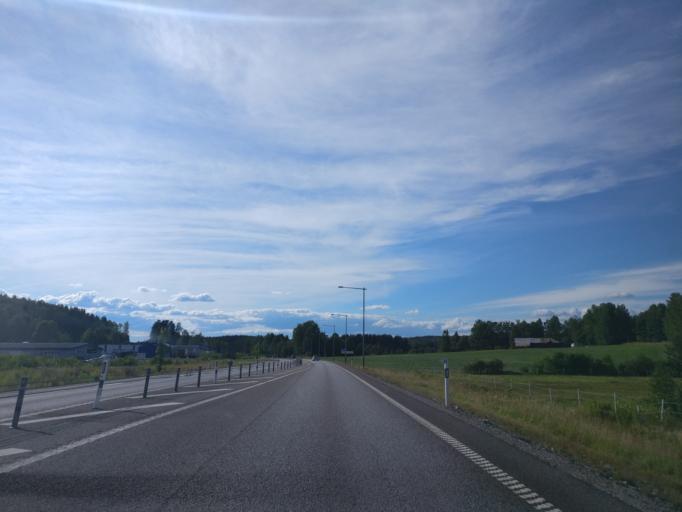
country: SE
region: Vaermland
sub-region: Arvika Kommun
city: Arvika
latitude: 59.6587
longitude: 12.6423
